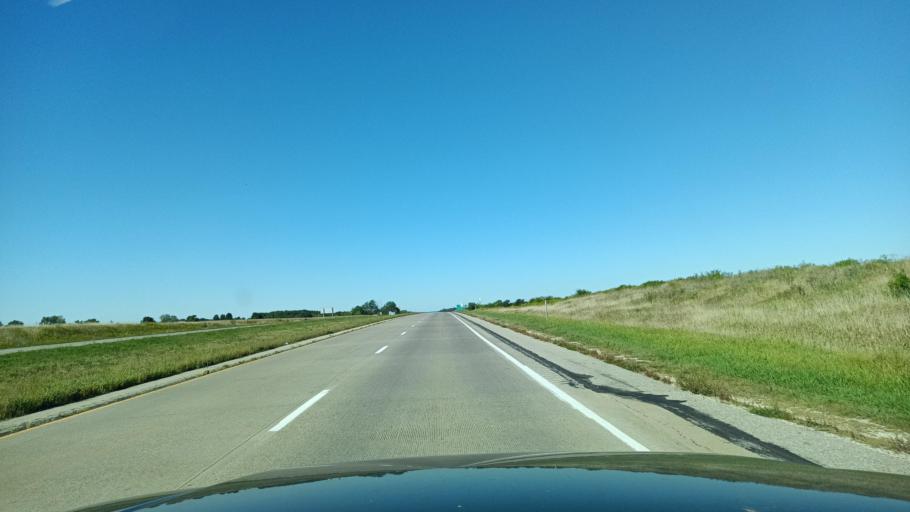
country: US
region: Iowa
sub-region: Lee County
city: Fort Madison
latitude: 40.6707
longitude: -91.3352
